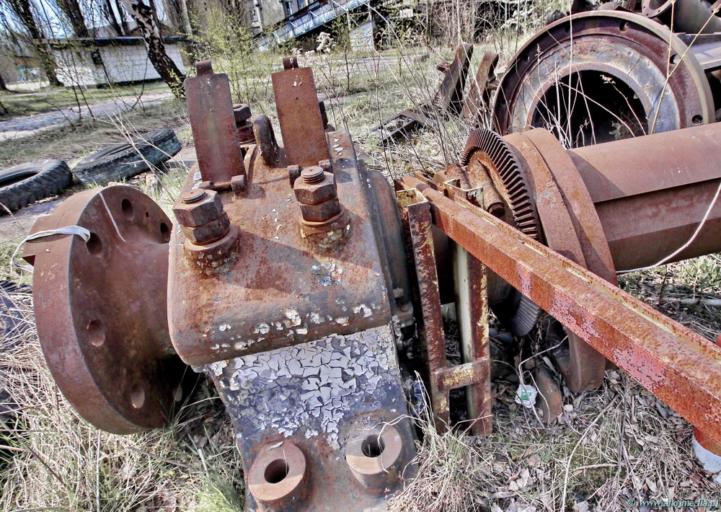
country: PL
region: Lower Silesian Voivodeship
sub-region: Powiat walbrzyski
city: Walbrzych
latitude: 50.7720
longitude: 16.2631
